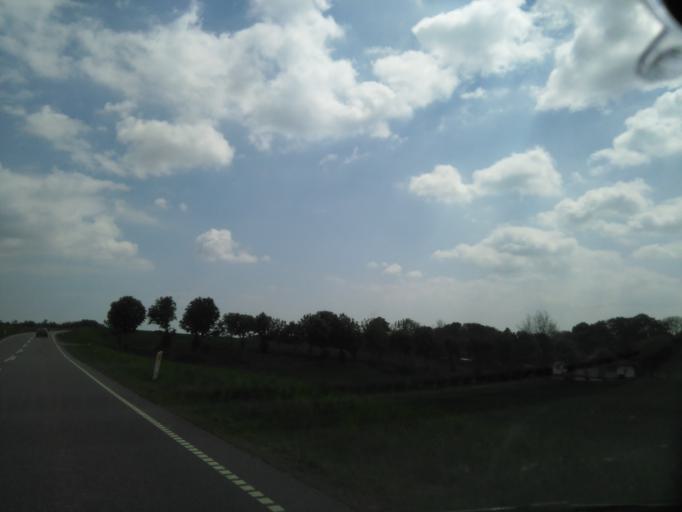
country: DK
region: Central Jutland
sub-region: Skanderborg Kommune
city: Stilling
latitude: 56.0006
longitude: 10.0054
